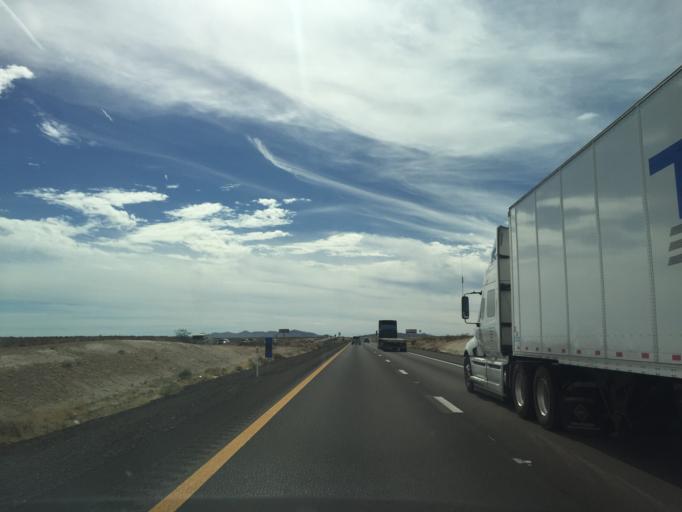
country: US
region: Nevada
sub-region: Clark County
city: Moapa Town
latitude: 36.5219
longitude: -114.7353
